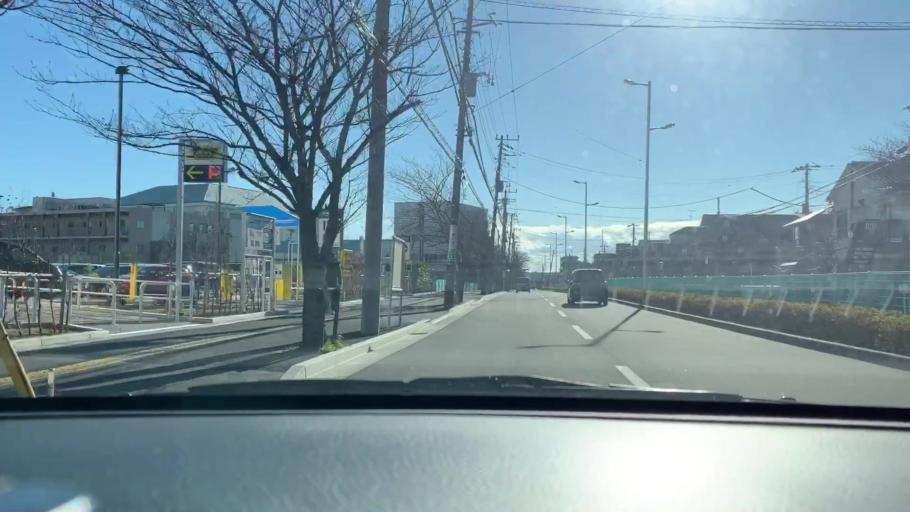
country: JP
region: Tokyo
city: Urayasu
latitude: 35.6475
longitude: 139.8926
